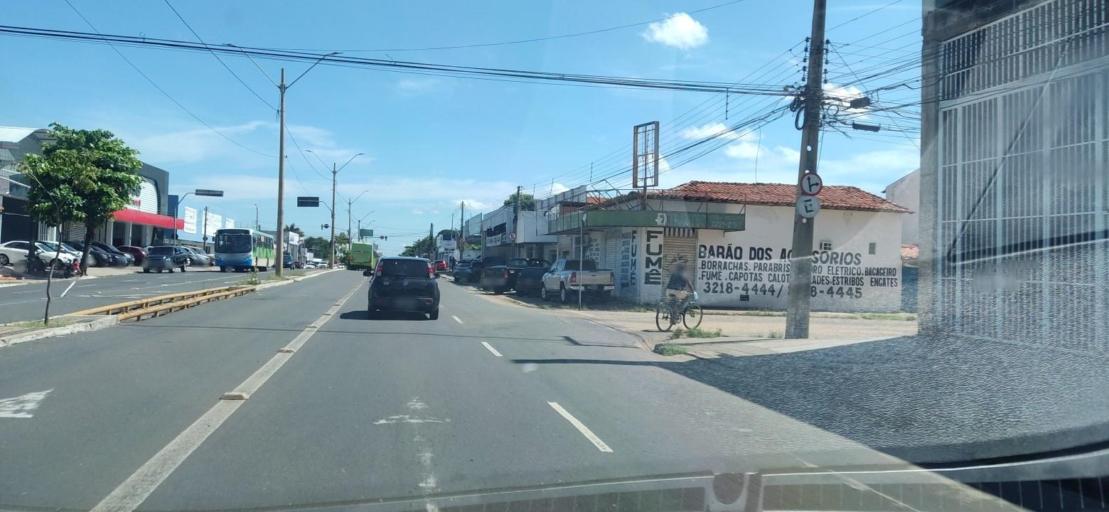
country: BR
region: Piaui
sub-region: Teresina
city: Teresina
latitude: -5.1073
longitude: -42.8085
